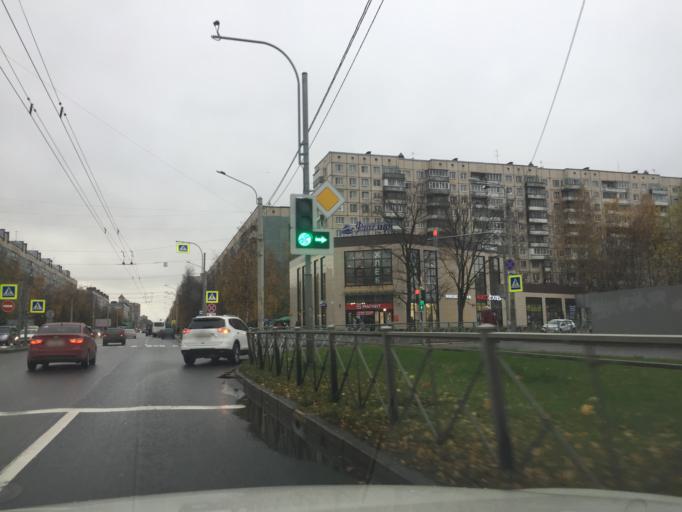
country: RU
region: Leningrad
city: Akademicheskoe
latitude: 60.0255
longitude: 30.3839
